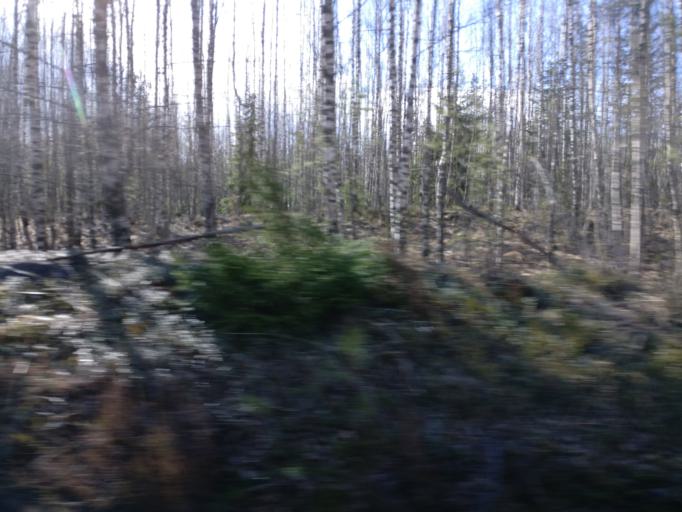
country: FI
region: Varsinais-Suomi
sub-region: Salo
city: Suomusjaervi
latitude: 60.3067
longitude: 23.6469
